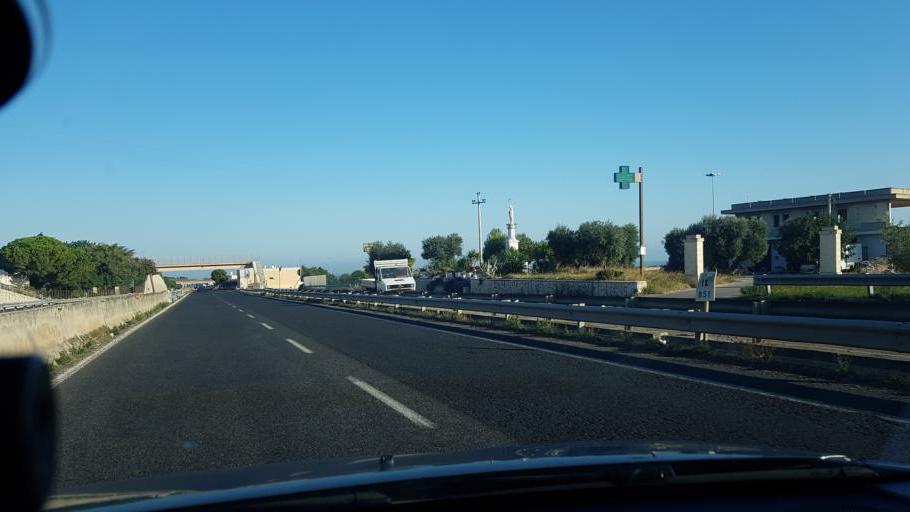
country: IT
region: Apulia
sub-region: Provincia di Brindisi
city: Fasano
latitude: 40.8886
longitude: 17.3340
